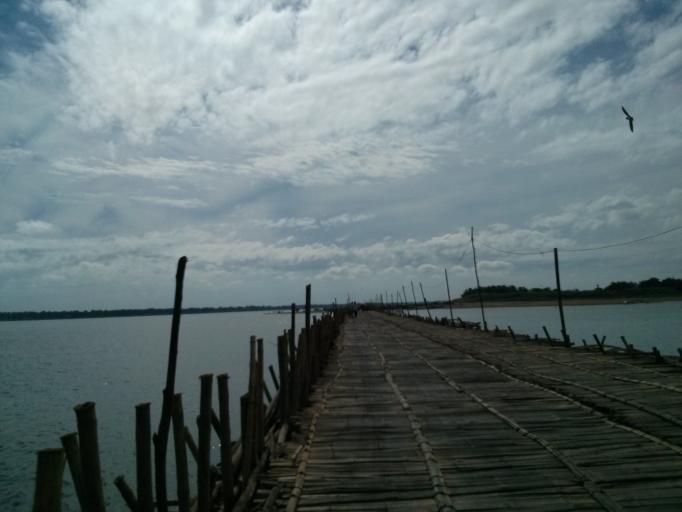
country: KH
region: Kampong Cham
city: Kampong Cham
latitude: 11.9757
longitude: 105.4619
